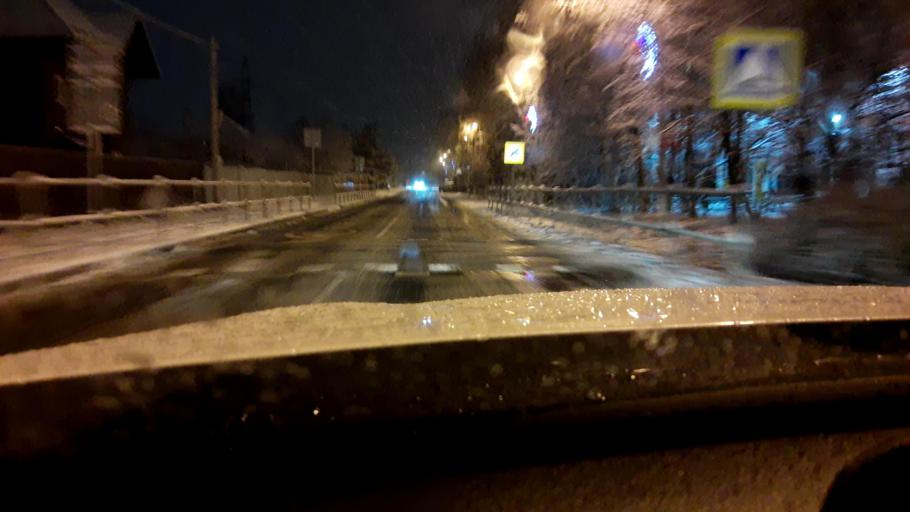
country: RU
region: Moskovskaya
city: Arkhangel'skoye
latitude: 55.7848
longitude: 37.3070
